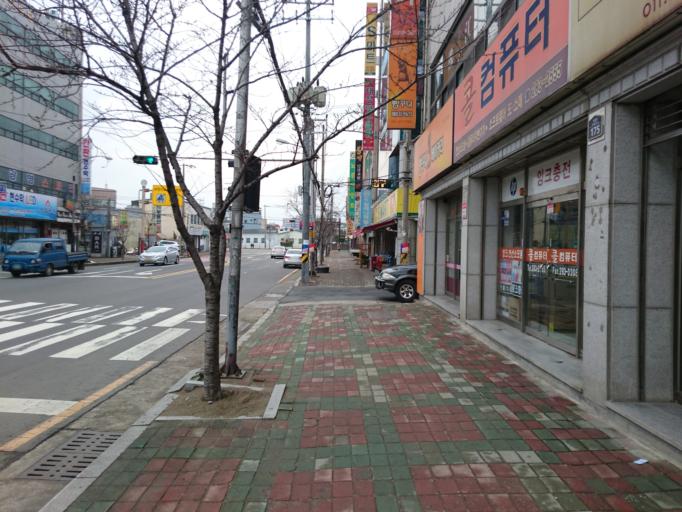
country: KR
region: Gyeongsangbuk-do
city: Pohang
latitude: 36.0219
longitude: 129.3652
